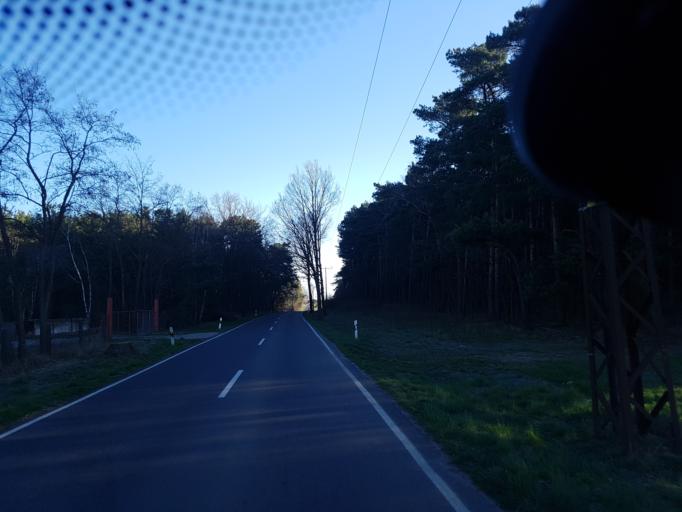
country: DE
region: Brandenburg
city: Jamlitz
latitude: 52.0505
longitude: 14.4260
